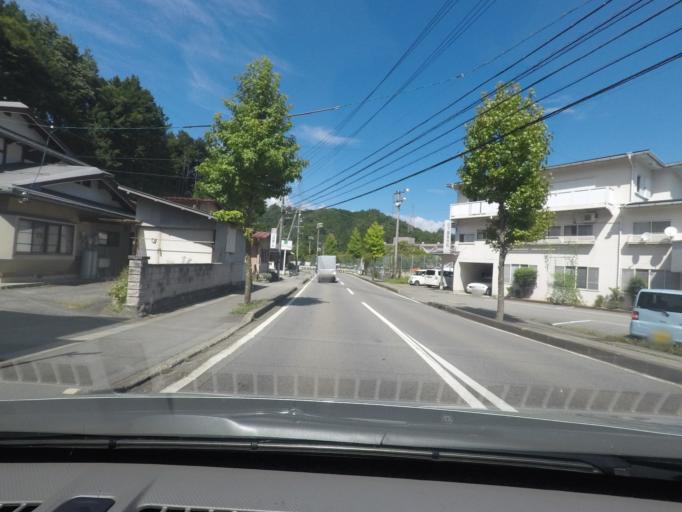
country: JP
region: Gifu
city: Takayama
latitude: 36.1501
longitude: 137.2749
